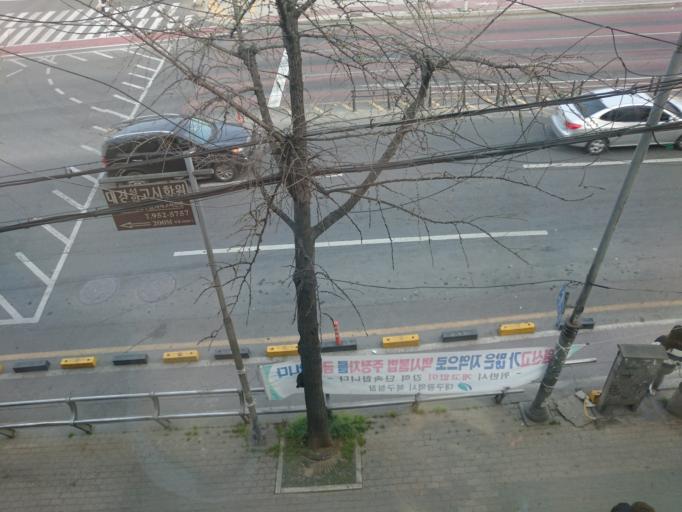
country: KR
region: Daegu
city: Daegu
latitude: 35.8926
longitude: 128.6089
